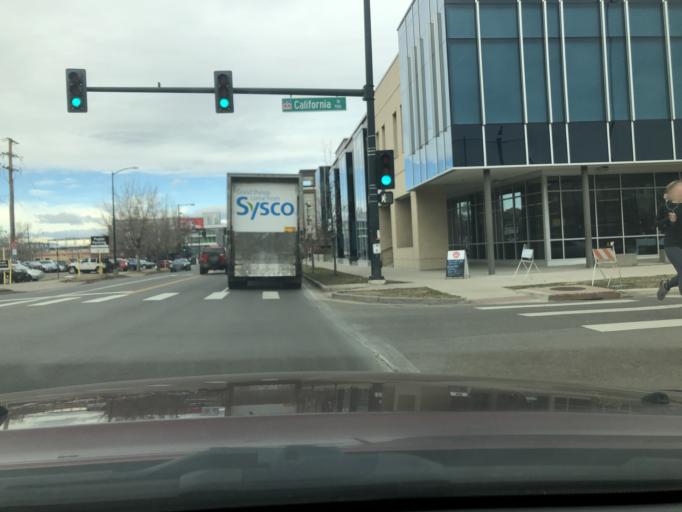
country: US
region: Colorado
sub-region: Denver County
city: Denver
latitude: 39.7517
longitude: -104.9836
